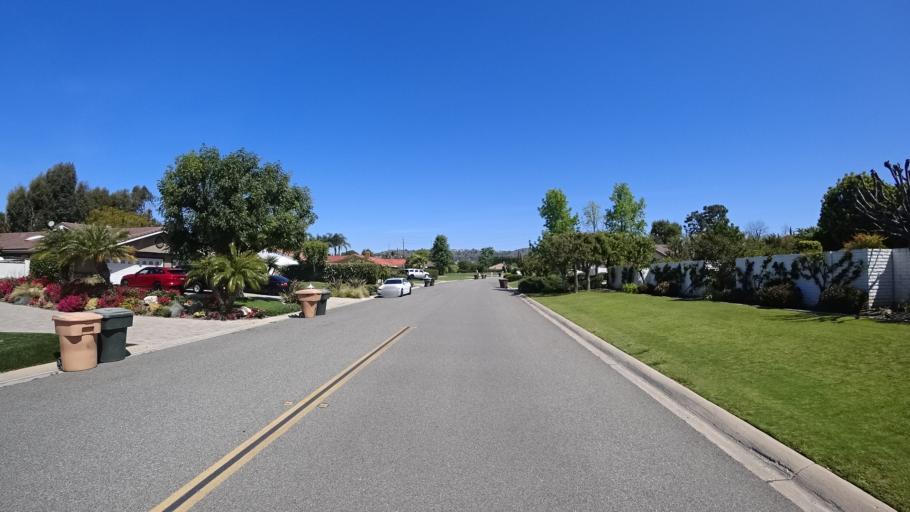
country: US
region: California
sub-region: Orange County
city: Villa Park
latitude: 33.8131
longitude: -117.8060
